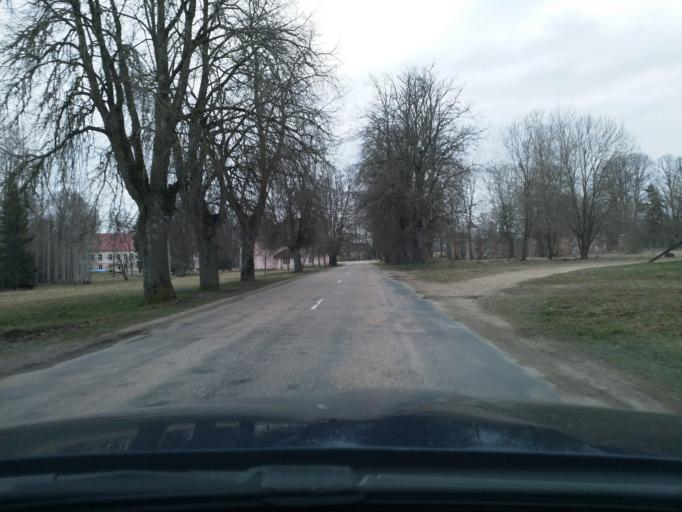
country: LV
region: Talsu Rajons
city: Sabile
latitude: 56.9257
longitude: 22.5628
